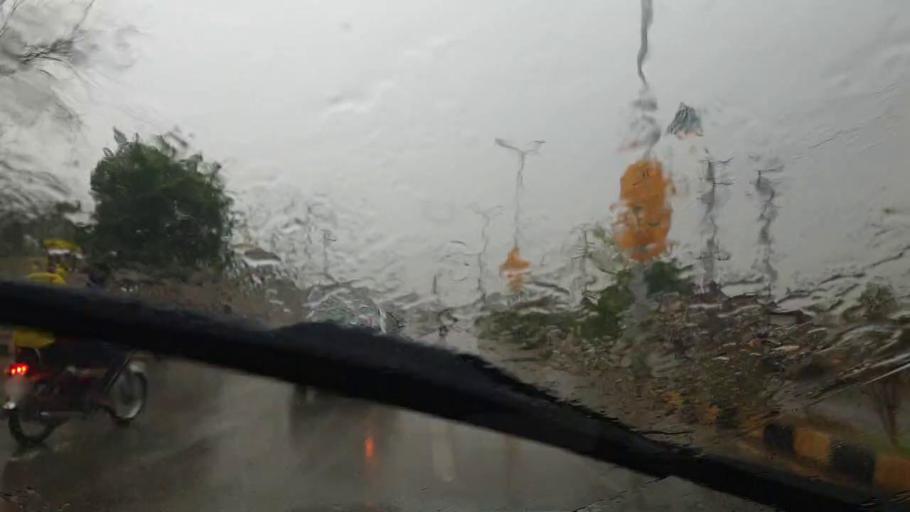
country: PK
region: Sindh
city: Sukkur
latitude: 27.6948
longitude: 68.8460
